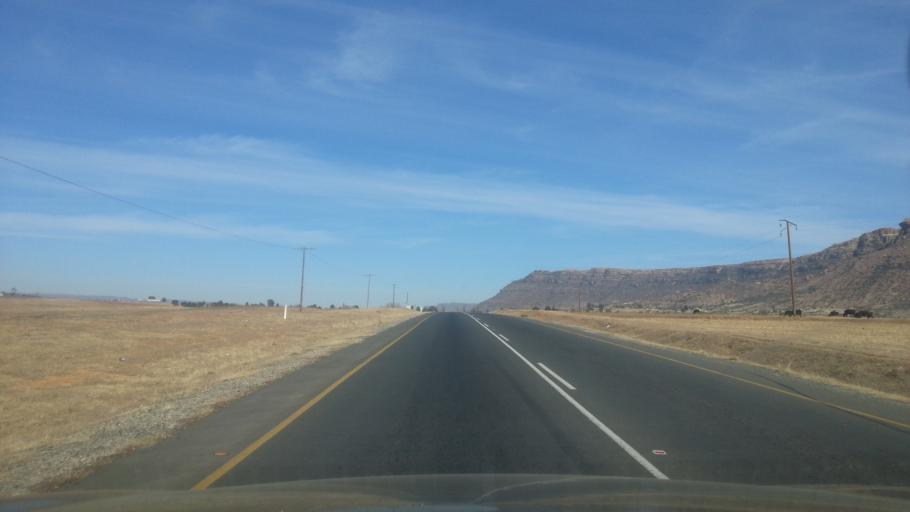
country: LS
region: Maseru
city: Maseru
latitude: -29.4727
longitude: 27.5323
